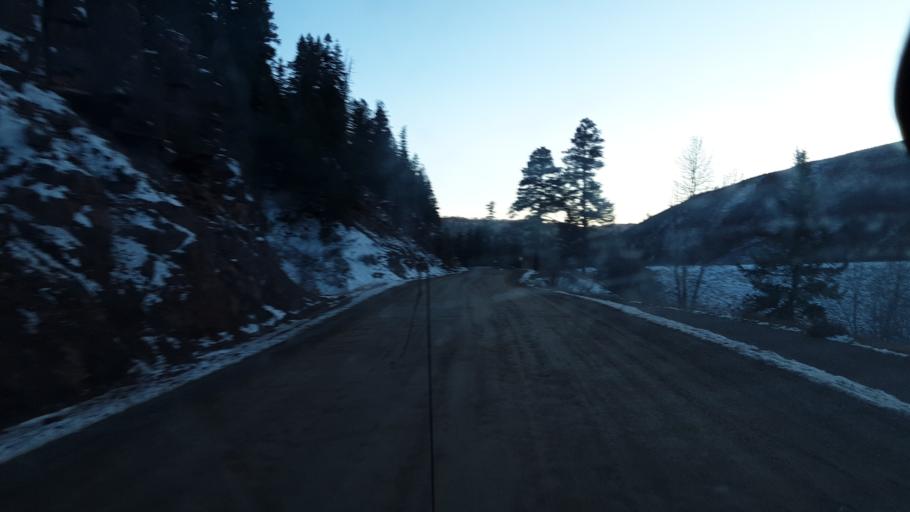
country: US
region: Colorado
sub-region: La Plata County
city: Bayfield
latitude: 37.3833
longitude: -107.6576
